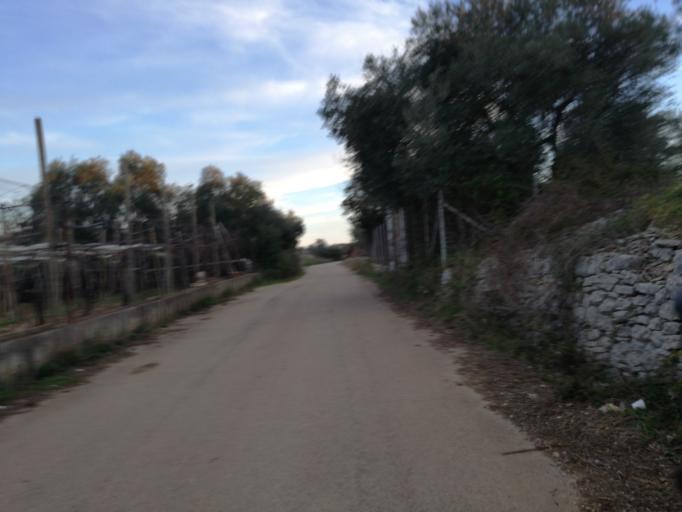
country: IT
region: Apulia
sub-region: Provincia di Bari
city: Adelfia
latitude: 41.0167
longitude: 16.8717
